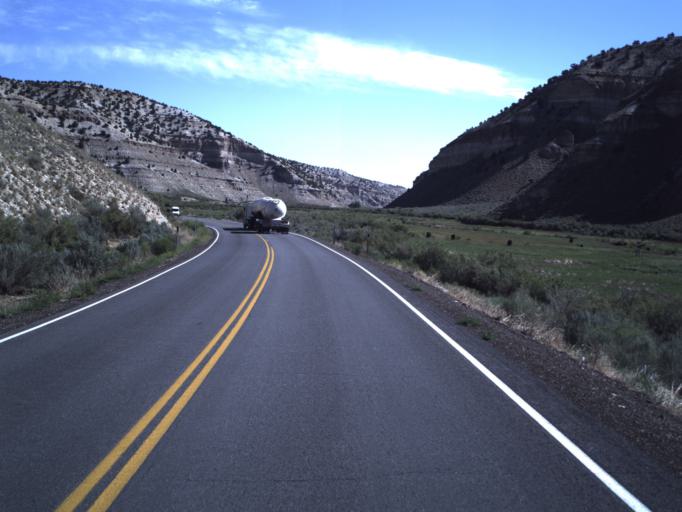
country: US
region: Utah
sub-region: Duchesne County
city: Duchesne
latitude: 40.0808
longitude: -110.4997
